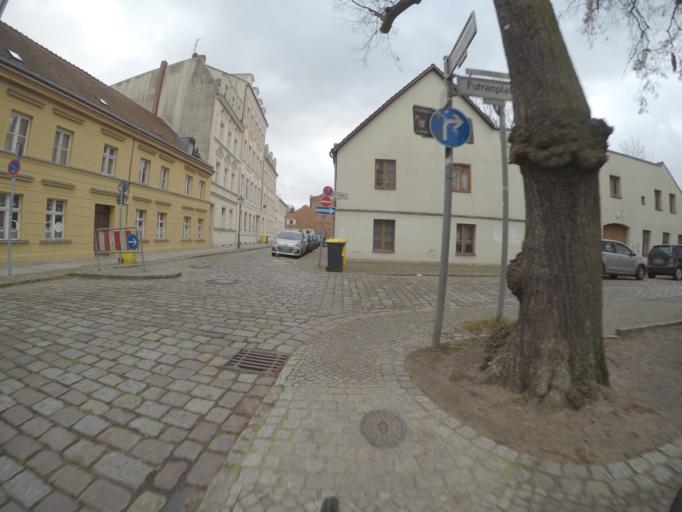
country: DE
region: Berlin
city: Kopenick Bezirk
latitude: 52.4466
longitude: 13.5790
